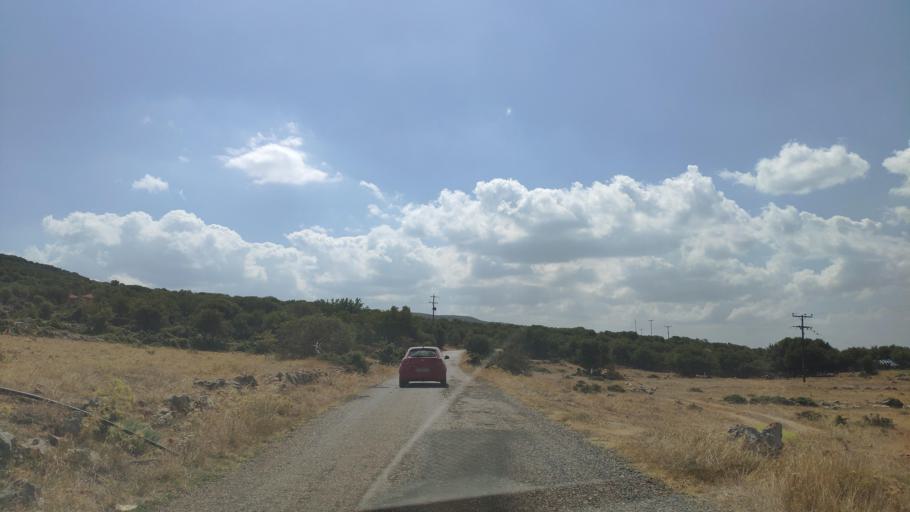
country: GR
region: Peloponnese
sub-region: Nomos Lakonias
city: Kariai
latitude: 37.3059
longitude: 22.4569
